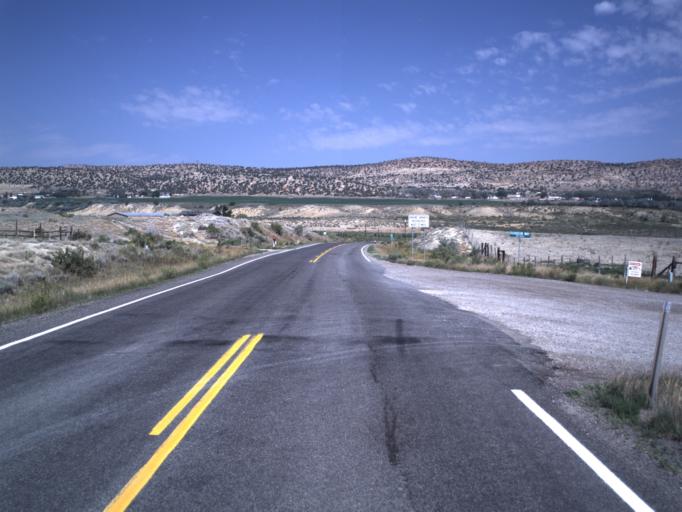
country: US
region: Utah
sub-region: Daggett County
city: Manila
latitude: 40.9734
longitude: -109.7196
